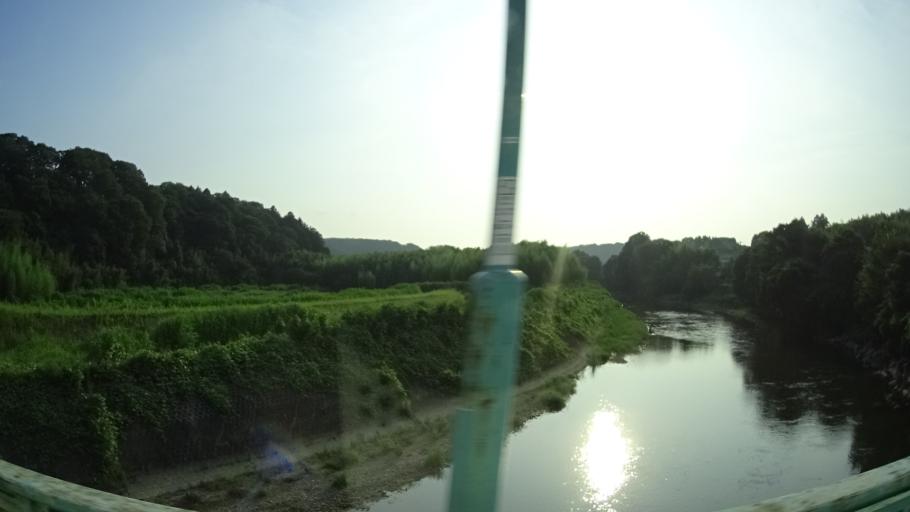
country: JP
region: Tochigi
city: Karasuyama
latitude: 36.6215
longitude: 140.1532
